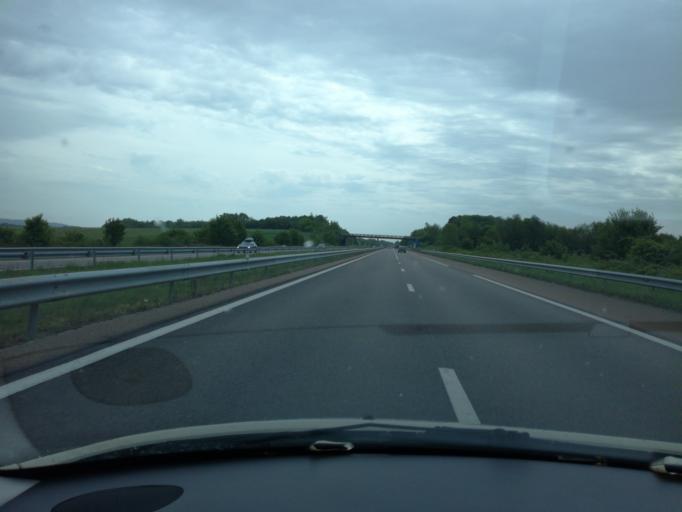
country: FR
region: Franche-Comte
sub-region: Departement du Jura
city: Mont-sous-Vaudrey
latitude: 46.8765
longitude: 5.5836
